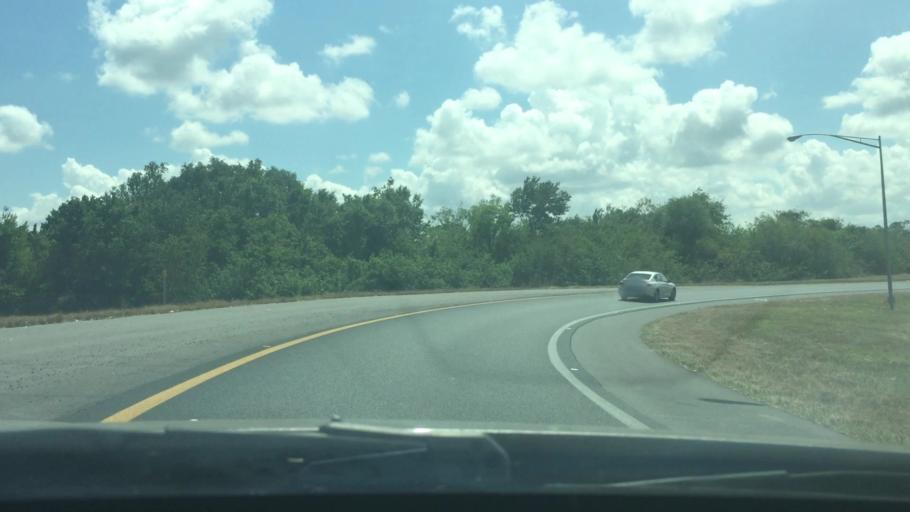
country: US
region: Florida
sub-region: Osceola County
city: Buenaventura Lakes
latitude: 28.2900
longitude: -81.3452
